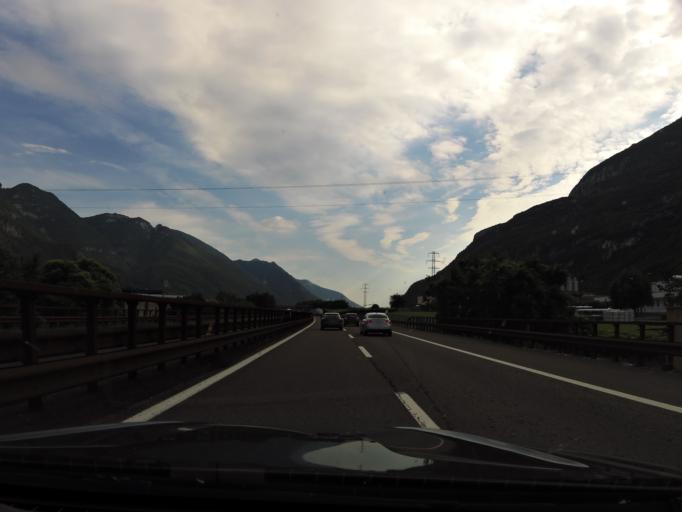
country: IT
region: Veneto
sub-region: Provincia di Verona
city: Rivalta
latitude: 45.6653
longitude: 10.8956
